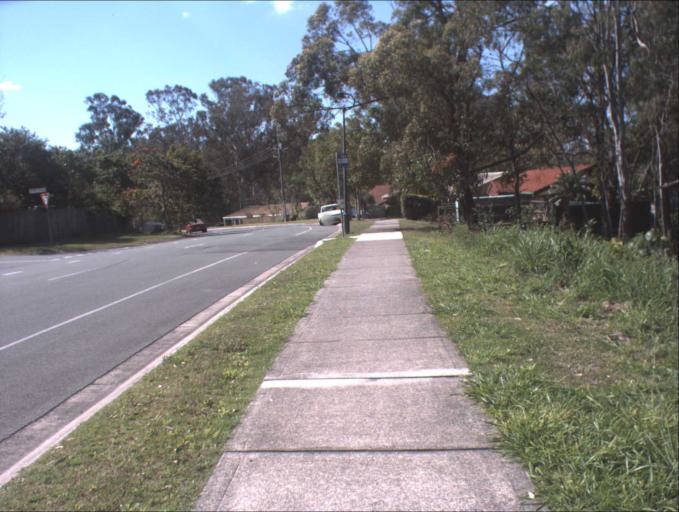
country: AU
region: Queensland
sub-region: Logan
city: Waterford West
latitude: -27.6990
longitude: 153.1613
